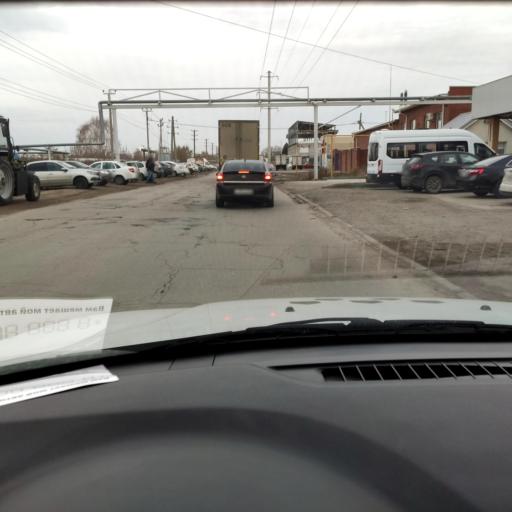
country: RU
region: Samara
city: Tol'yatti
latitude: 53.5436
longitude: 49.4400
